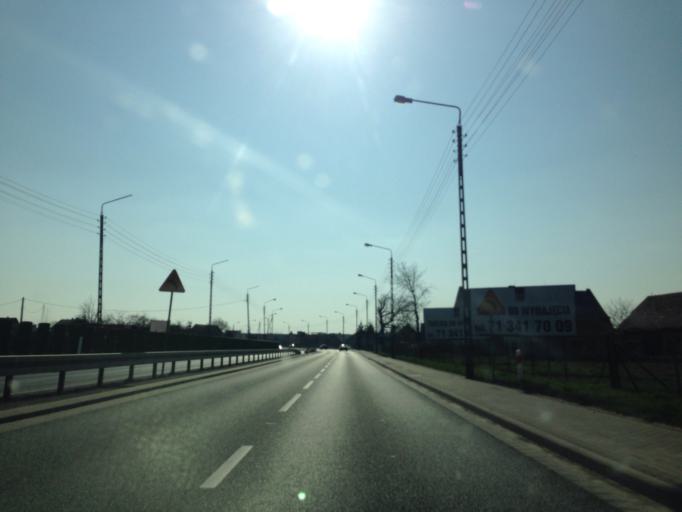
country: PL
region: Lower Silesian Voivodeship
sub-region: Powiat wroclawski
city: Dlugoleka
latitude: 51.1900
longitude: 17.2317
